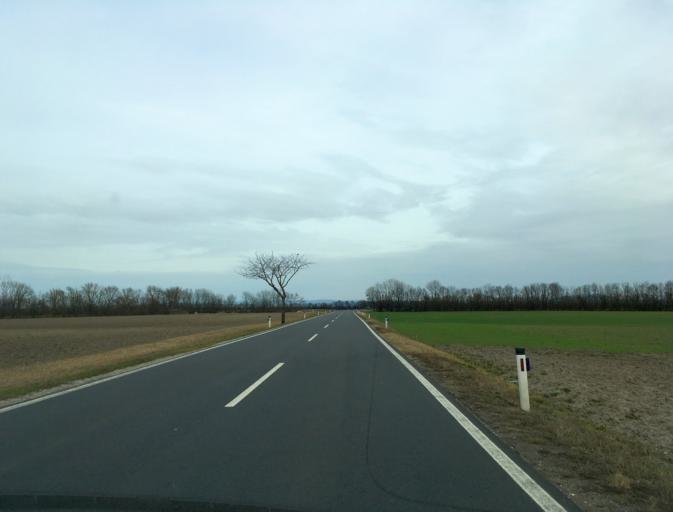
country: AT
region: Lower Austria
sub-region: Politischer Bezirk Ganserndorf
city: Untersiebenbrunn
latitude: 48.2223
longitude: 16.7576
